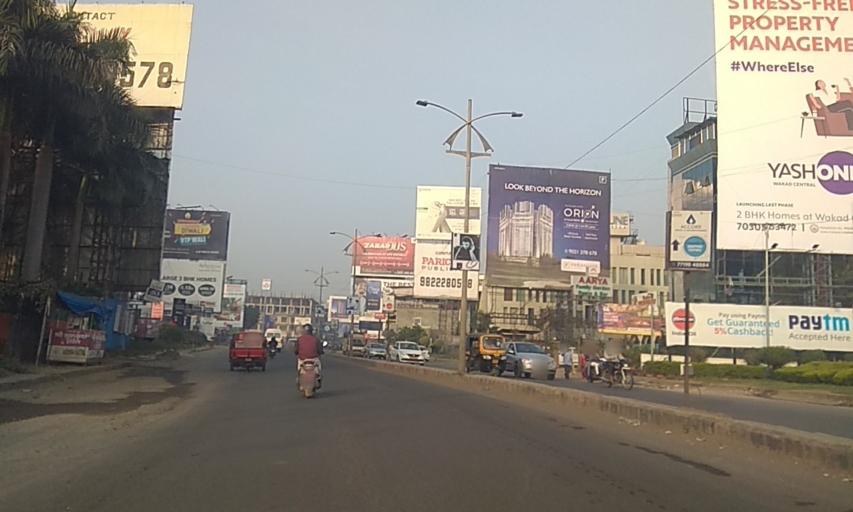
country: IN
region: Maharashtra
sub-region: Pune Division
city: Pimpri
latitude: 18.5909
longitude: 73.7490
